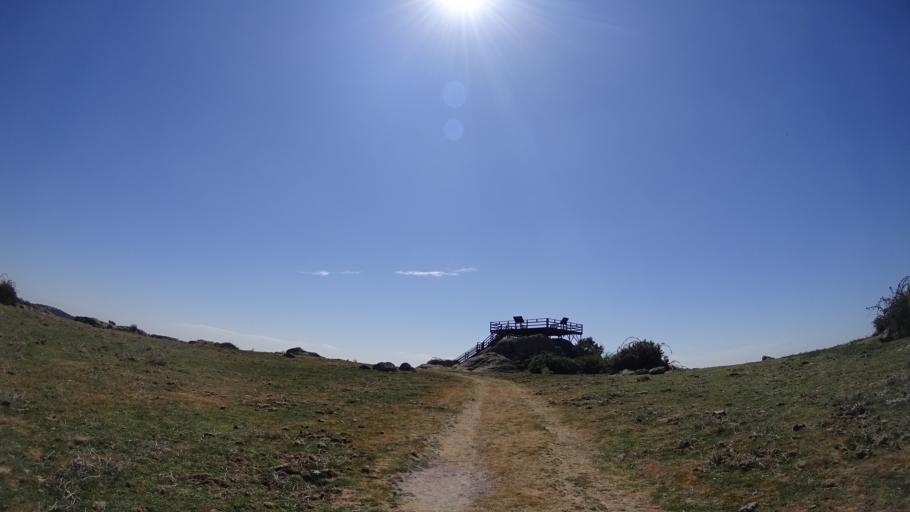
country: ES
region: Madrid
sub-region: Provincia de Madrid
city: Colmenar Viejo
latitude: 40.7063
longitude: -3.7497
